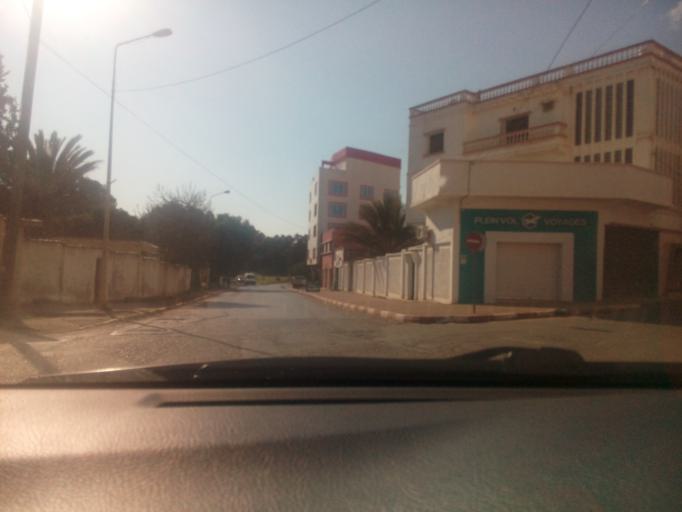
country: DZ
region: Oran
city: Oran
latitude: 35.7027
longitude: -0.6074
